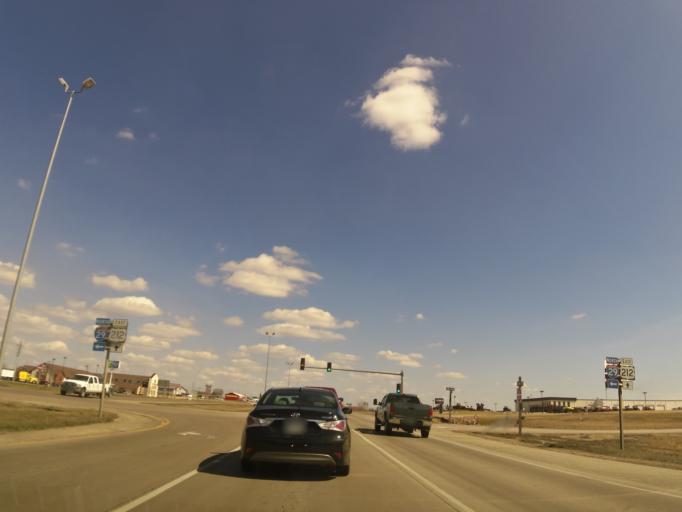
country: US
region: South Dakota
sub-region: Codington County
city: Watertown
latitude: 44.8900
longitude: -97.0561
